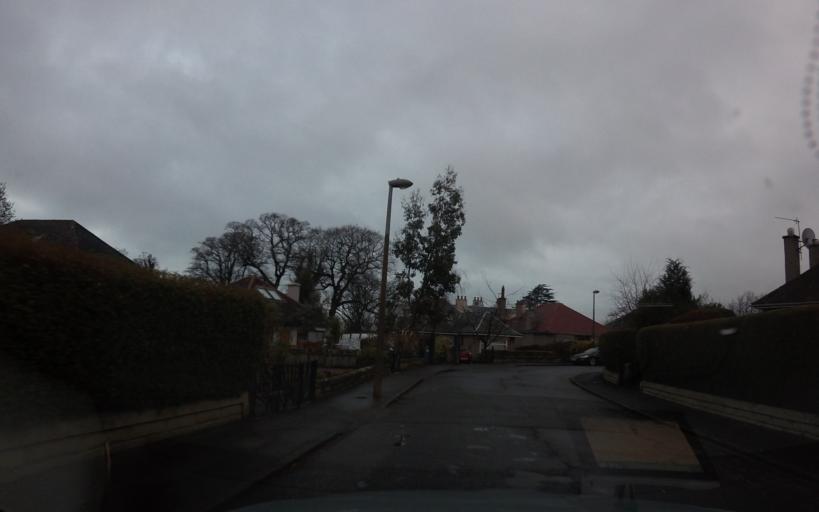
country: GB
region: Scotland
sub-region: Edinburgh
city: Colinton
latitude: 55.9198
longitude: -3.2476
